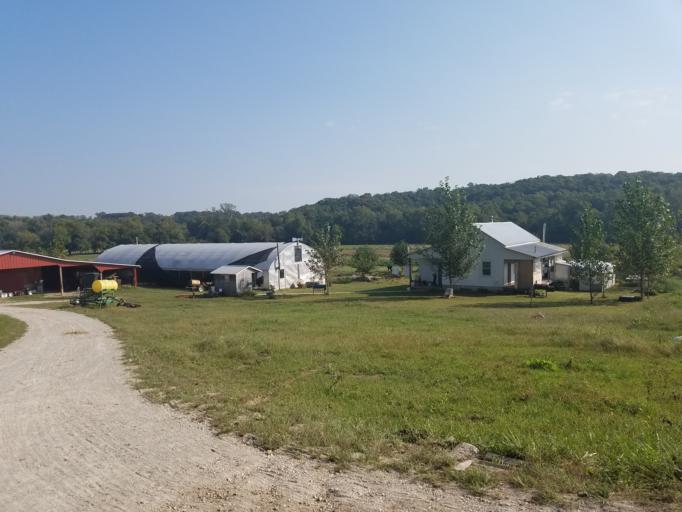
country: US
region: Missouri
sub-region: Moniteau County
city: California
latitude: 38.7367
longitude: -92.6236
